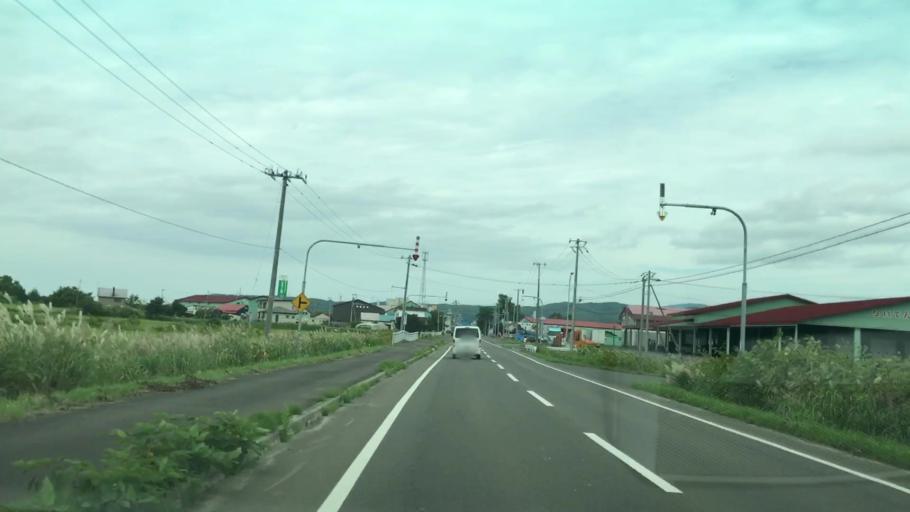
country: JP
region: Hokkaido
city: Iwanai
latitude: 43.0130
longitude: 140.5724
